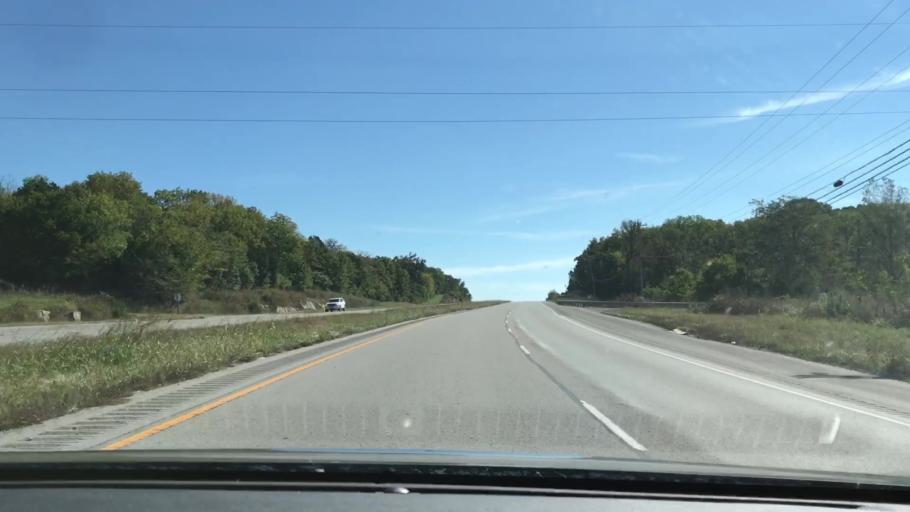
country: US
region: Kentucky
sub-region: Logan County
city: Russellville
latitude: 36.8423
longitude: -86.8292
